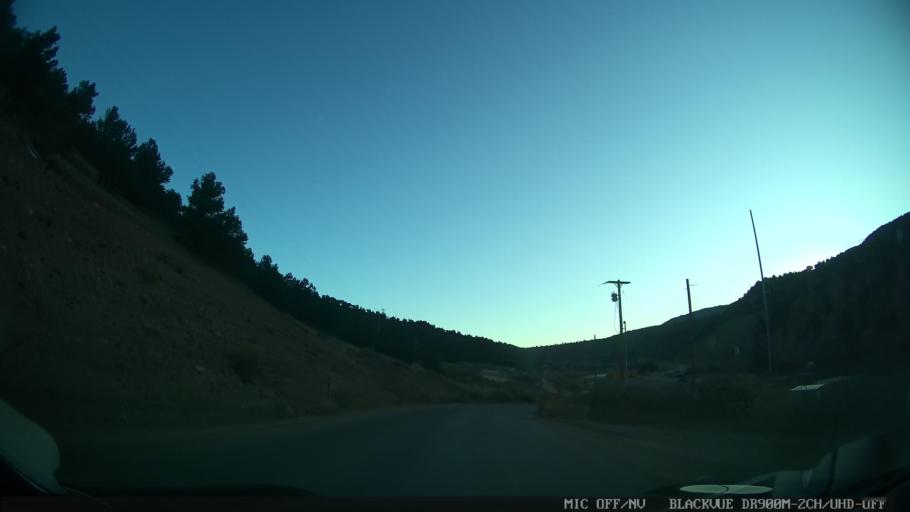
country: US
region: Colorado
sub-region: Eagle County
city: Edwards
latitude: 39.8897
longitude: -106.6198
